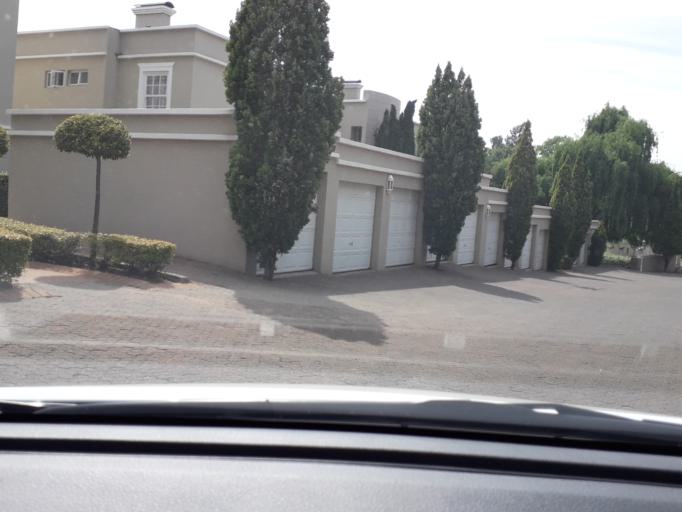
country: ZA
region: Gauteng
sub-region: City of Johannesburg Metropolitan Municipality
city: Modderfontein
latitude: -26.1022
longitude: 28.0650
